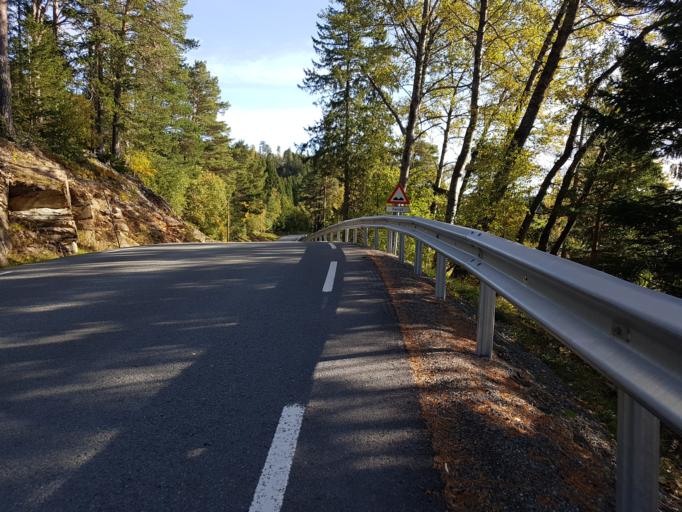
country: NO
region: Sor-Trondelag
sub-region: Malvik
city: Malvik
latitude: 63.3682
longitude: 10.6183
